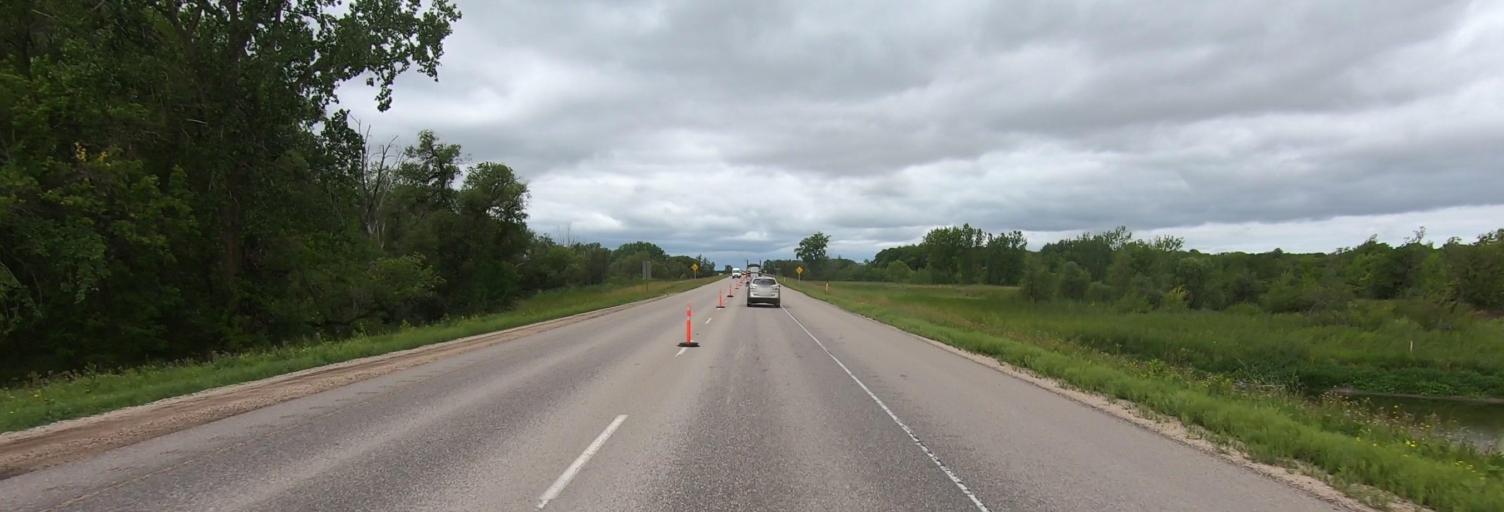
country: CA
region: Manitoba
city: Portage la Prairie
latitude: 49.9699
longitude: -98.0928
